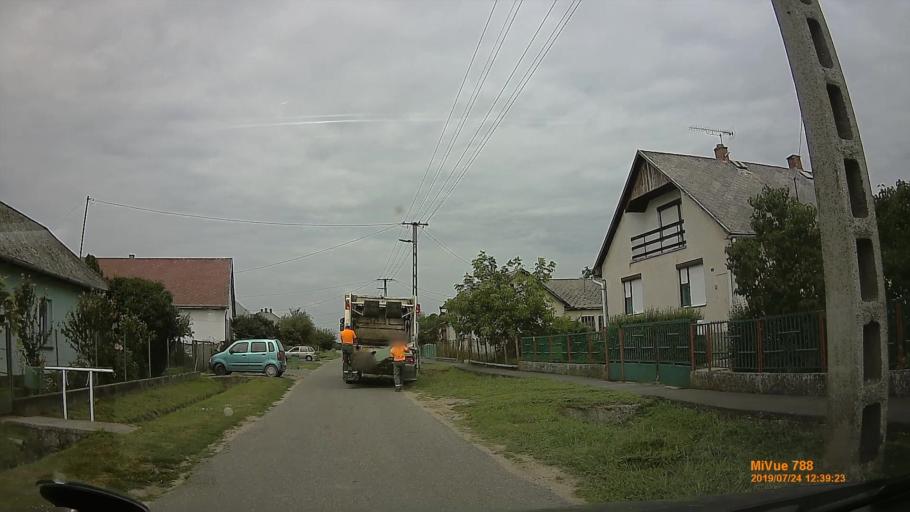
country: HU
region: Szabolcs-Szatmar-Bereg
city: Aranyosapati
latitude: 48.1883
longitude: 22.3135
